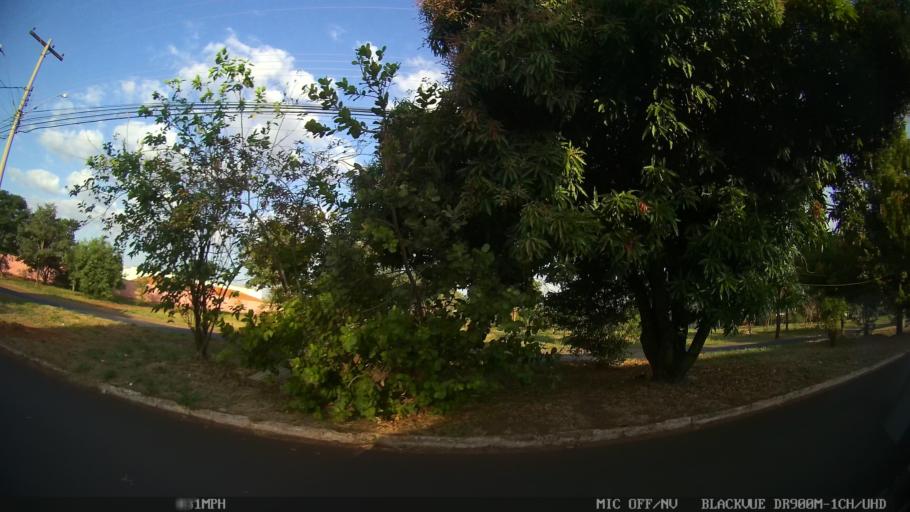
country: BR
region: Sao Paulo
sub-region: Ribeirao Preto
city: Ribeirao Preto
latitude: -21.1643
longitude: -47.7455
